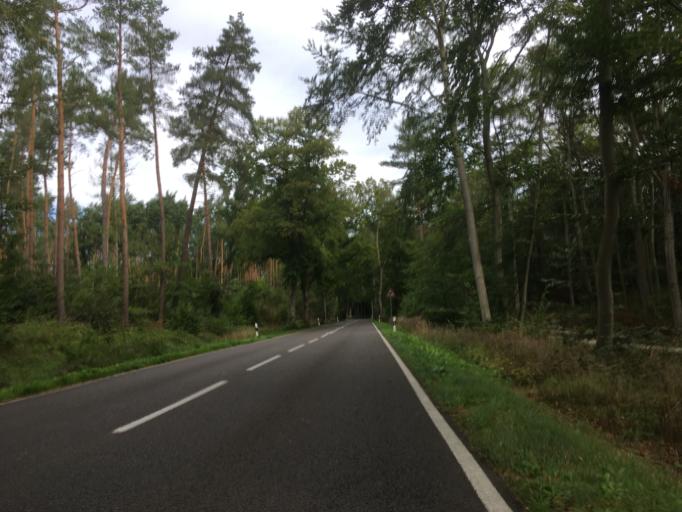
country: DE
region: Brandenburg
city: Templin
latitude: 53.1496
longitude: 13.5491
